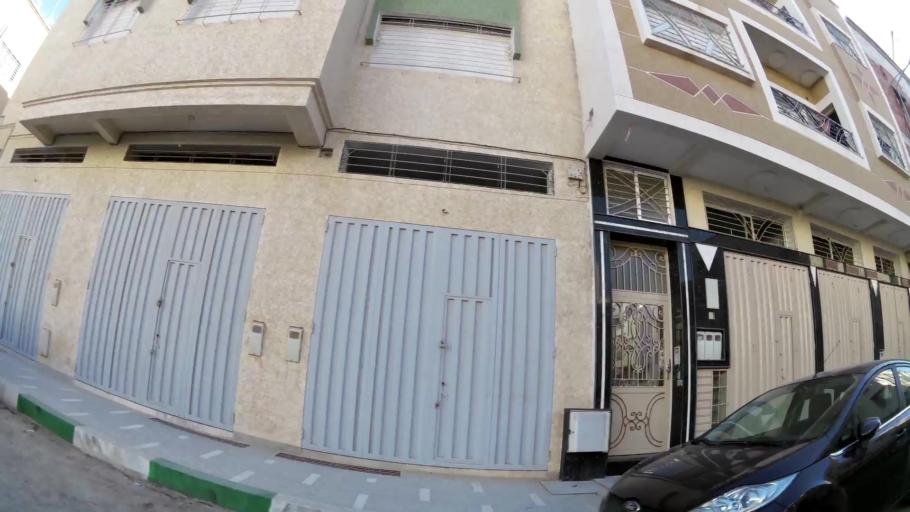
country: MA
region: Fes-Boulemane
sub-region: Fes
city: Fes
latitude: 34.0091
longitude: -5.0119
